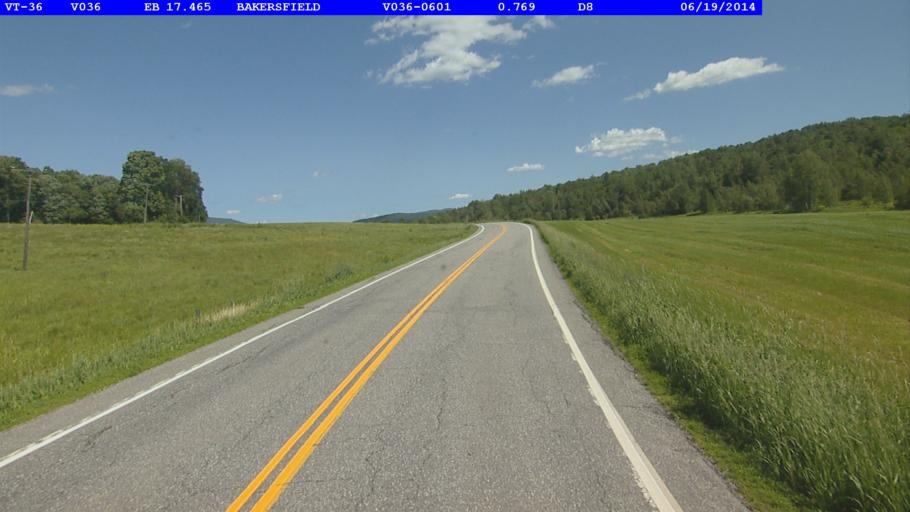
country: US
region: Vermont
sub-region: Franklin County
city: Enosburg Falls
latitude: 44.7841
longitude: -72.8345
